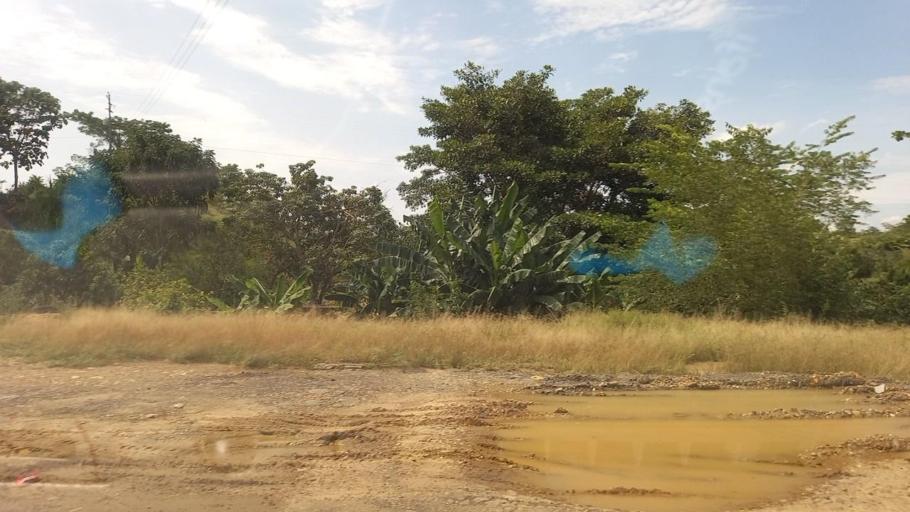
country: CO
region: Antioquia
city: Puerto Berrio
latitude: 6.3392
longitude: -74.4325
